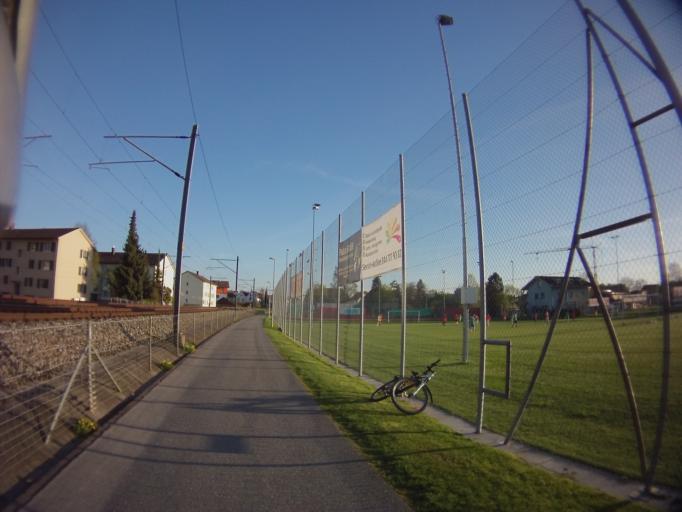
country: CH
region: Zurich
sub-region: Bezirk Affoltern
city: Affoltern / Unterdorf
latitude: 47.2849
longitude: 8.4520
